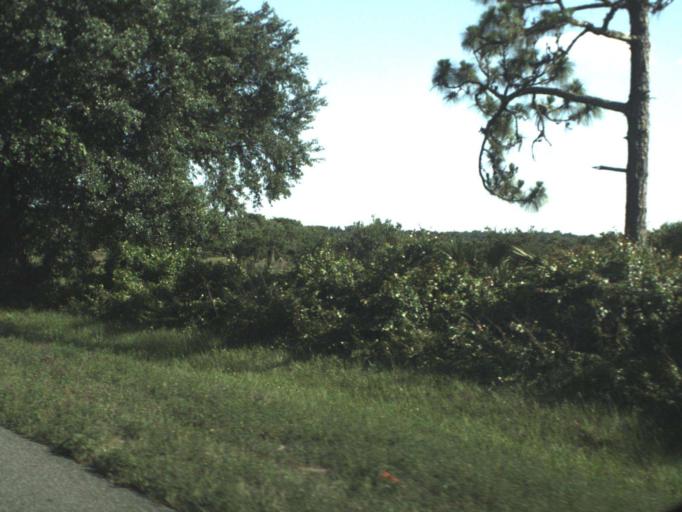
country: US
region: Florida
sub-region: Seminole County
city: Geneva
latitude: 28.7586
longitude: -81.1433
